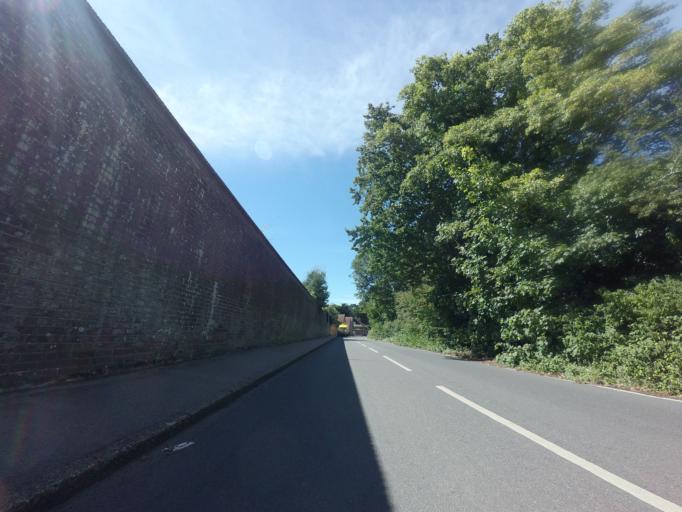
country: GB
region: England
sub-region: Kent
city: Sandwich
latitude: 51.2725
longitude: 1.3507
